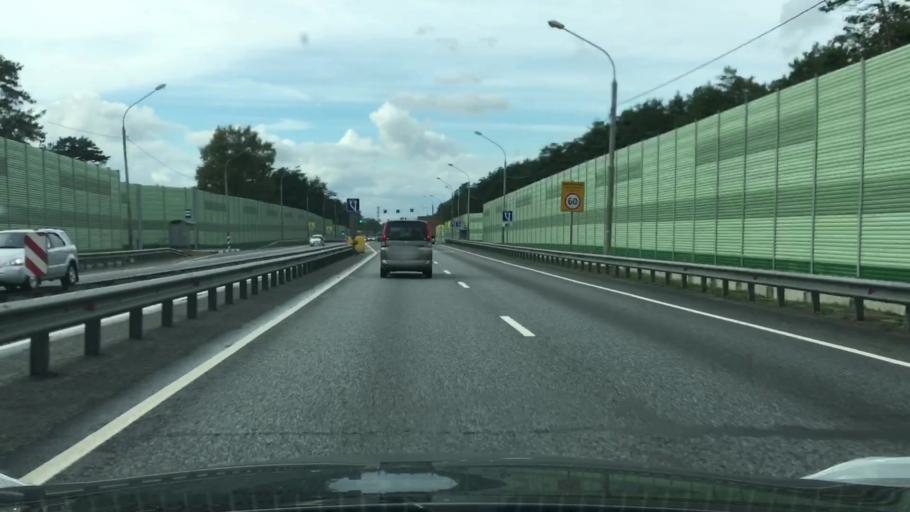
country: RU
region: Tverskaya
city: Radchenko
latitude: 56.6783
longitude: 36.3948
